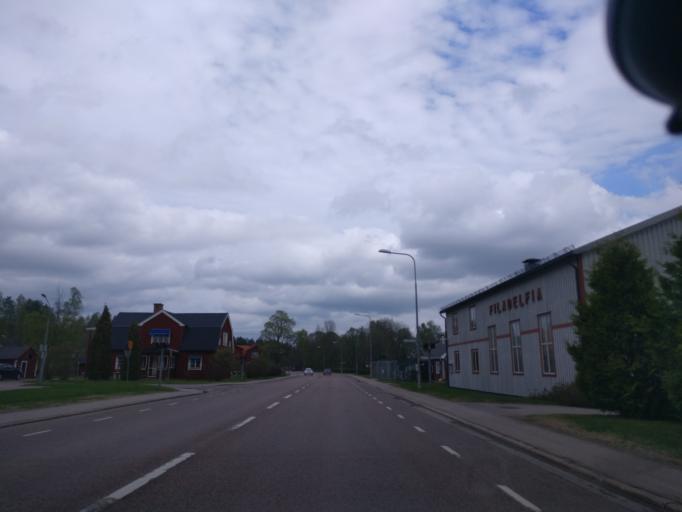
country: SE
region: Vaermland
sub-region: Hagfors Kommun
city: Ekshaerad
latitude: 60.1780
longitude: 13.4961
